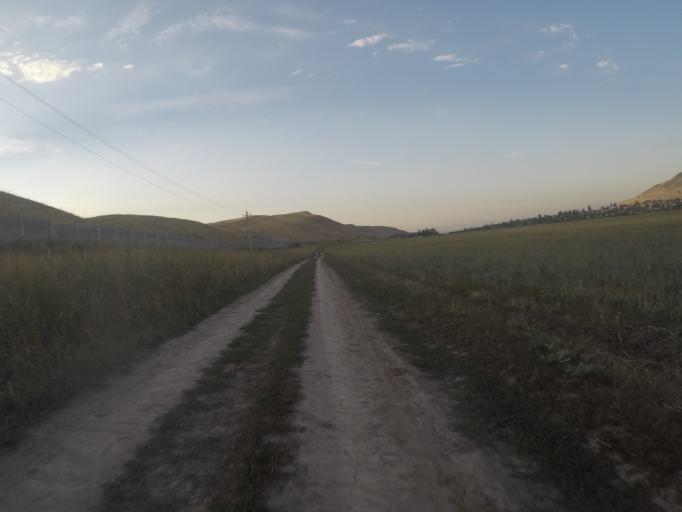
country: KG
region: Chuy
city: Bishkek
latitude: 42.7571
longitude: 74.6362
